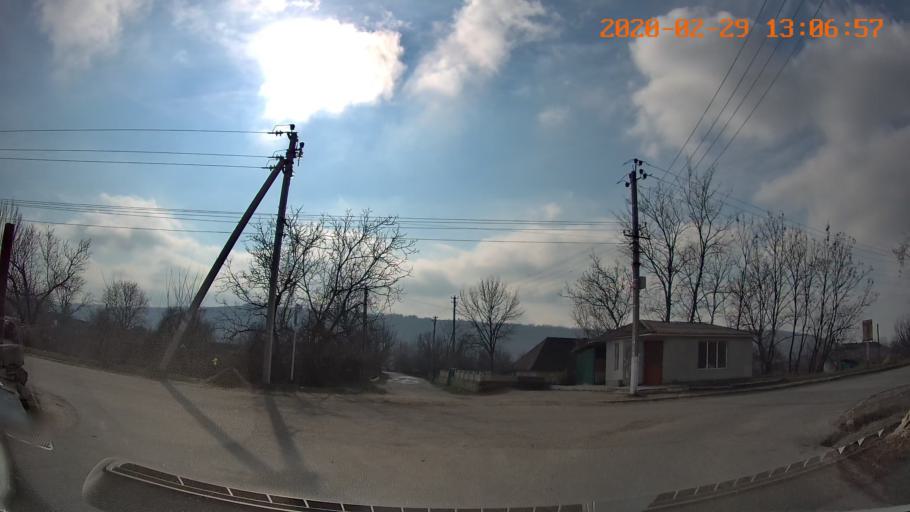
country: MD
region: Telenesti
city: Camenca
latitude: 48.0107
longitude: 28.7060
